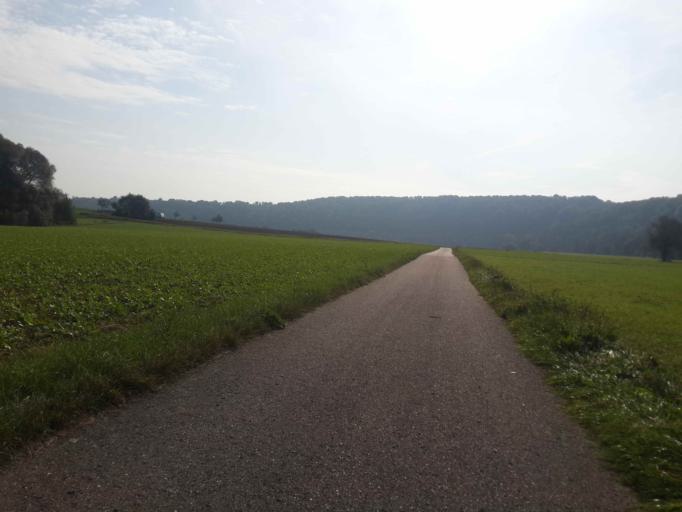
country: DE
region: Baden-Wuerttemberg
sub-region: Regierungsbezirk Stuttgart
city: Neudenau
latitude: 49.2749
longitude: 9.2359
